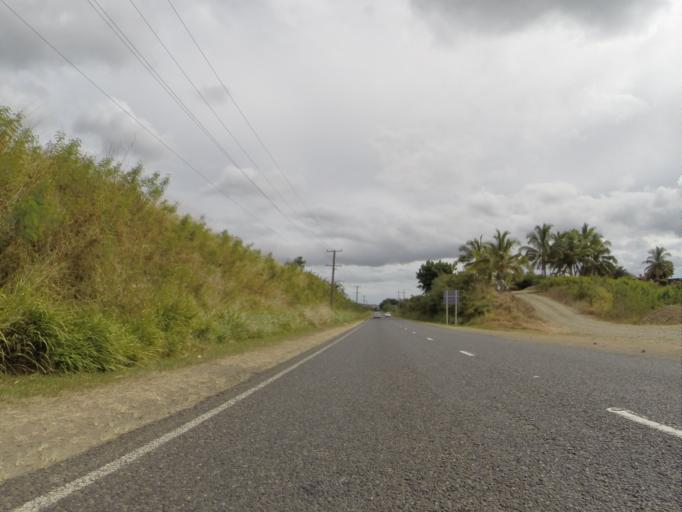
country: FJ
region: Western
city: Nadi
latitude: -18.0509
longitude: 177.3480
